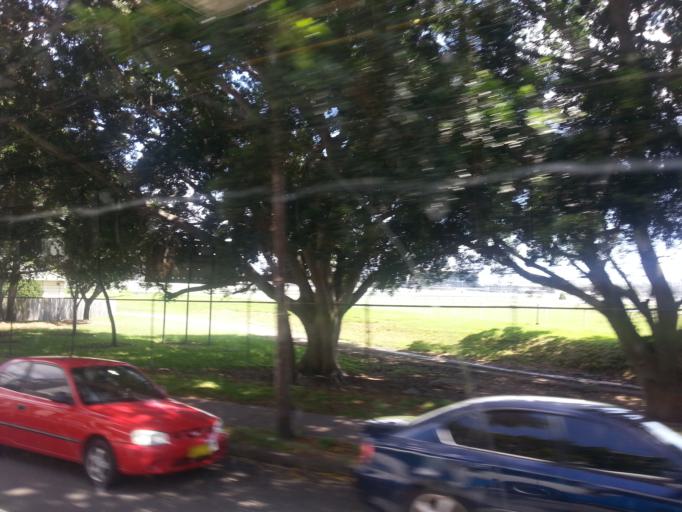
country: AU
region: New South Wales
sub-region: Randwick
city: Kingsford
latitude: -33.9155
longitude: 151.2305
